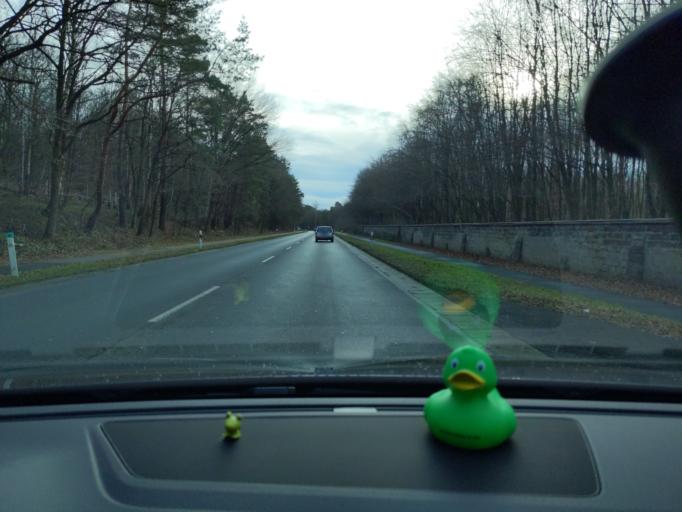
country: DE
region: North Rhine-Westphalia
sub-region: Regierungsbezirk Koln
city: Rath
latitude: 50.9052
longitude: 7.0994
